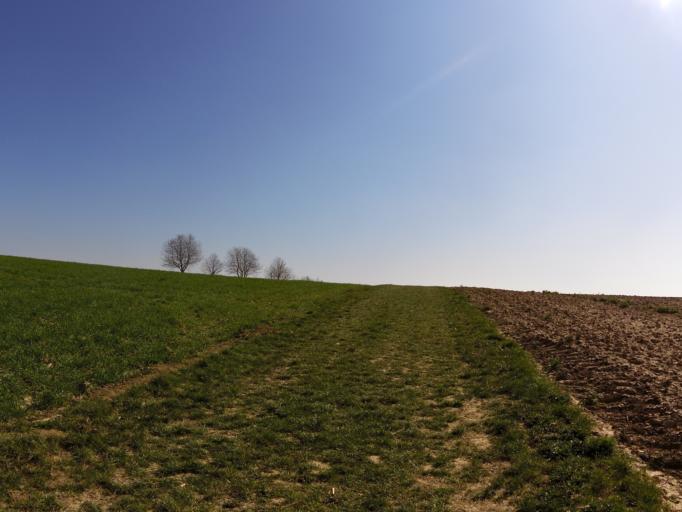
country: DE
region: Bavaria
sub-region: Regierungsbezirk Unterfranken
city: Kurnach
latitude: 49.8369
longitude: 10.0401
